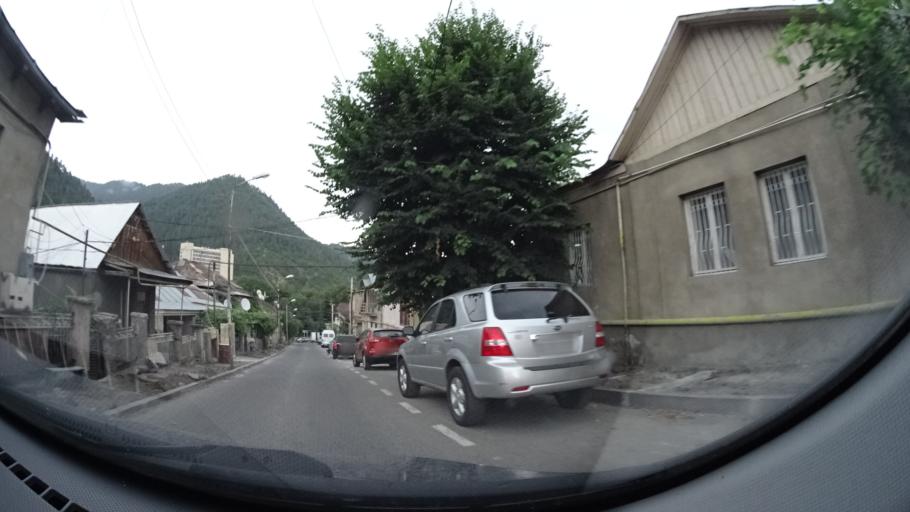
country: GE
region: Samtskhe-Javakheti
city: Borjomi
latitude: 41.8403
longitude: 43.3823
